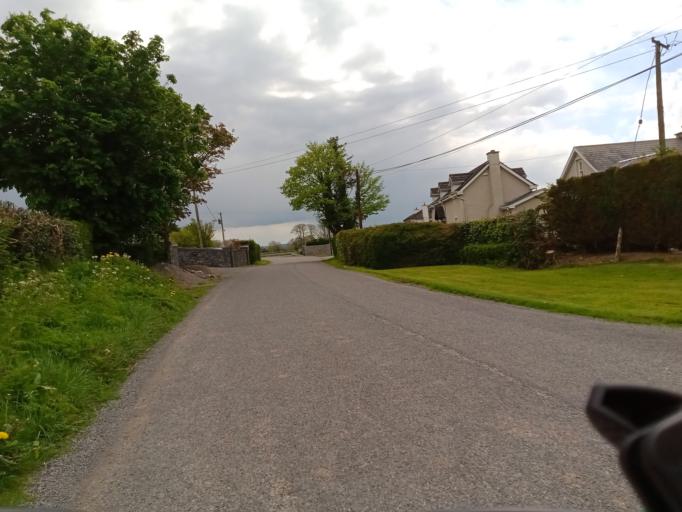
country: IE
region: Leinster
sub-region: Kilkenny
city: Kilkenny
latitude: 52.6116
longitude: -7.2928
